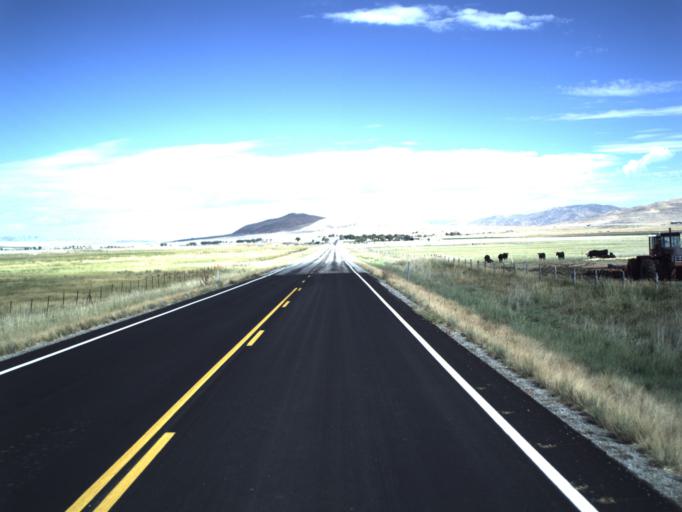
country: US
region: Utah
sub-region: Box Elder County
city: Tremonton
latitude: 41.7525
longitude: -112.4346
